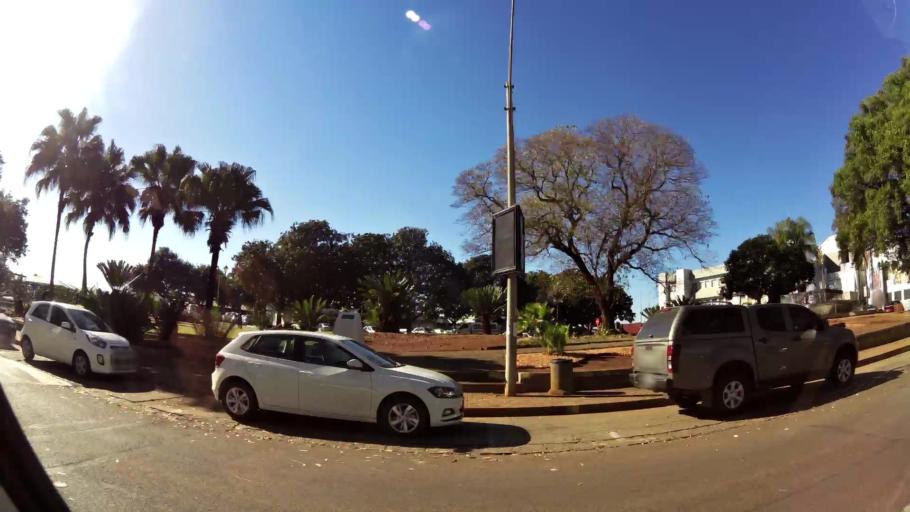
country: ZA
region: Limpopo
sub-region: Mopani District Municipality
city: Tzaneen
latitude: -23.8289
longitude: 30.1583
